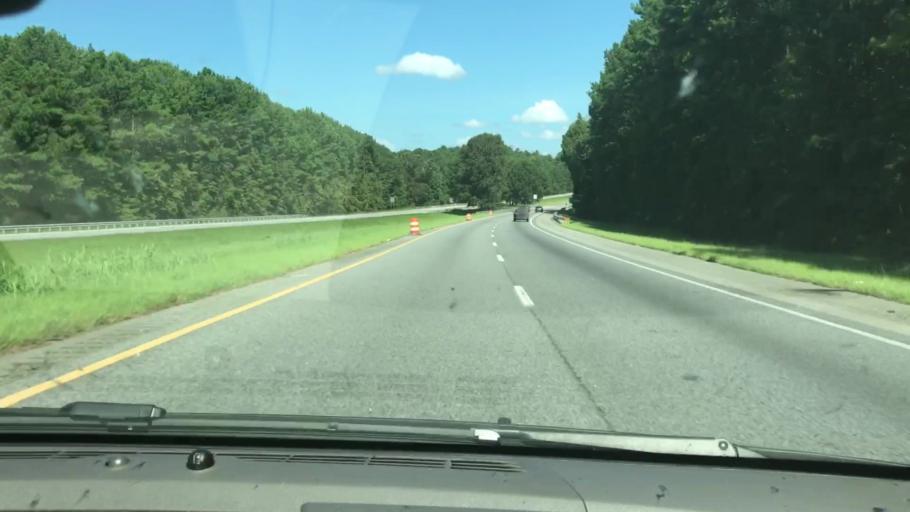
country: US
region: Georgia
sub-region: Harris County
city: Hamilton
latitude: 32.6353
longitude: -84.9662
